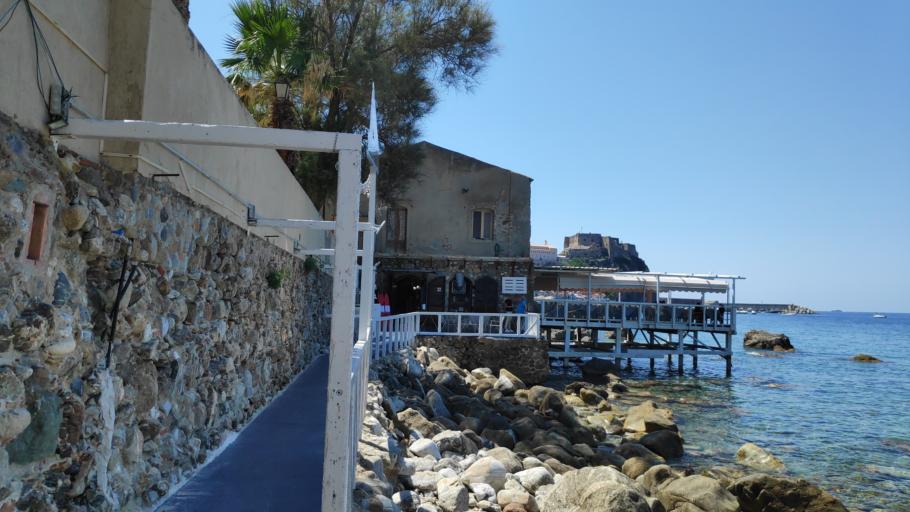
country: IT
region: Calabria
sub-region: Provincia di Reggio Calabria
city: Scilla
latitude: 38.2538
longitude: 15.7223
